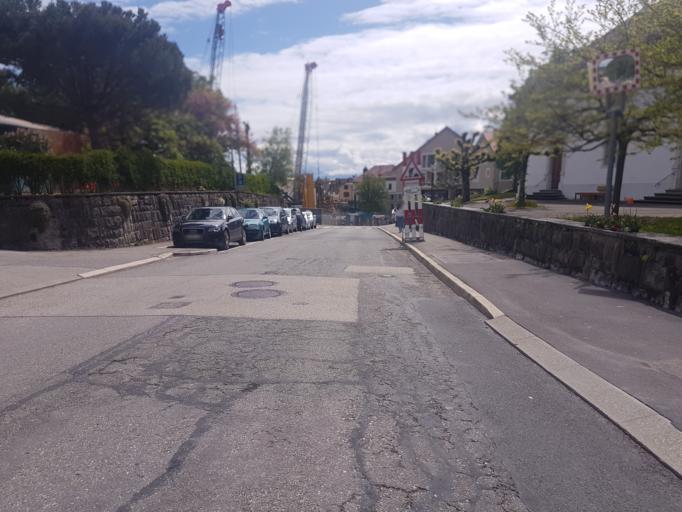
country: CH
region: Vaud
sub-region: Nyon District
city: Rolle
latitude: 46.4588
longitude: 6.3357
